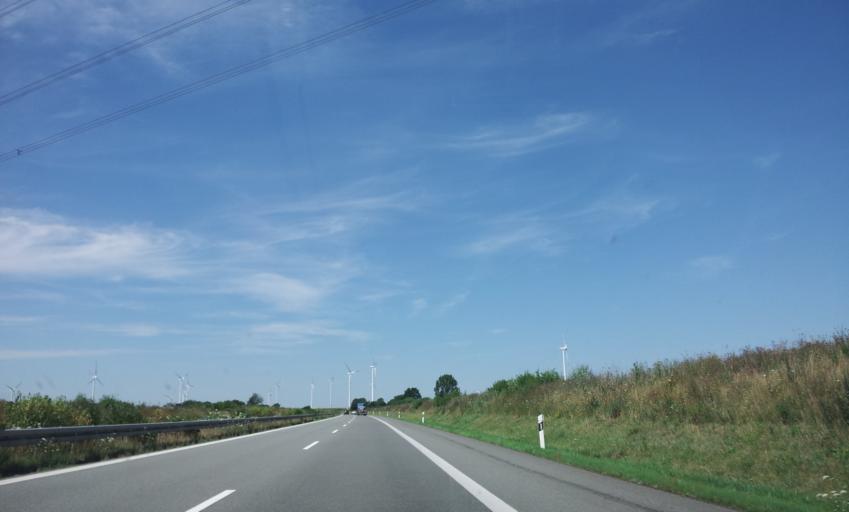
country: DE
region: Mecklenburg-Vorpommern
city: Dersekow
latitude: 54.0383
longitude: 13.2693
